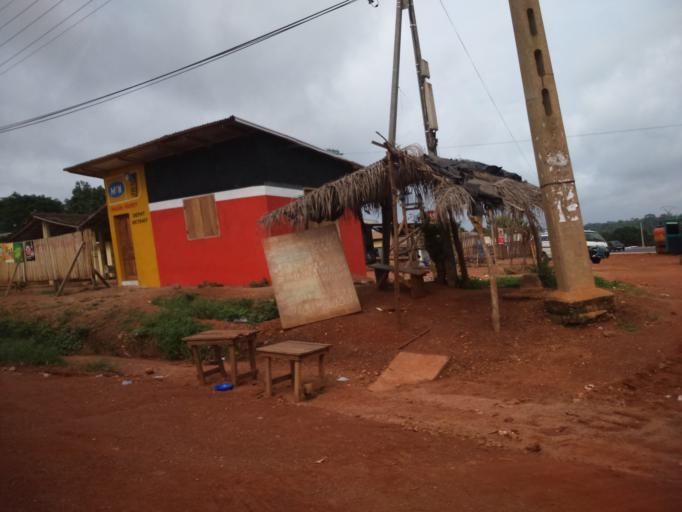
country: CI
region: Moyen-Comoe
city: Abengourou
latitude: 6.7195
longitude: -3.5154
